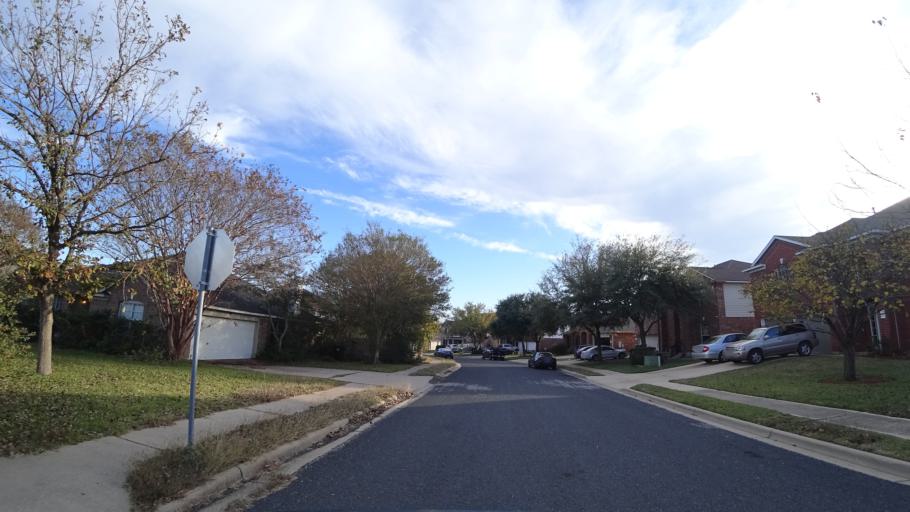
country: US
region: Texas
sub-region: Williamson County
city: Brushy Creek
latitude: 30.5017
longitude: -97.7358
